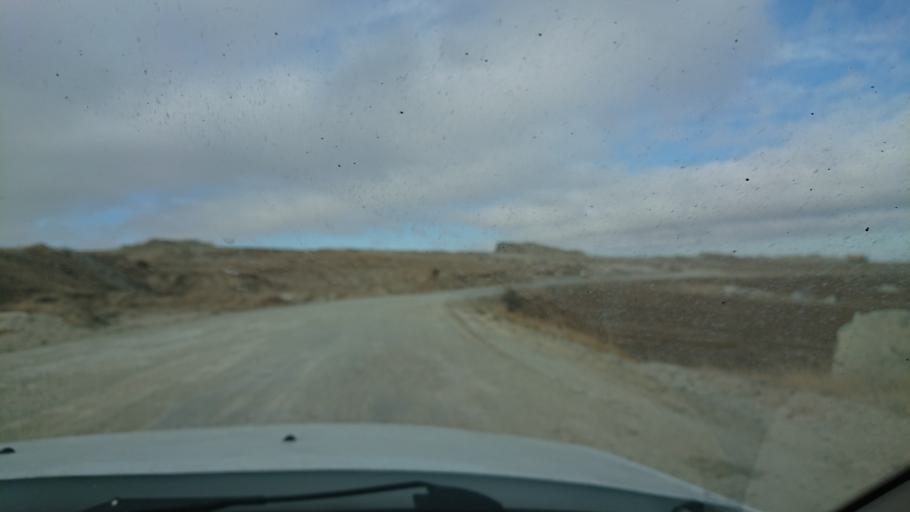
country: TR
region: Aksaray
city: Ortakoy
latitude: 38.7798
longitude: 34.0057
